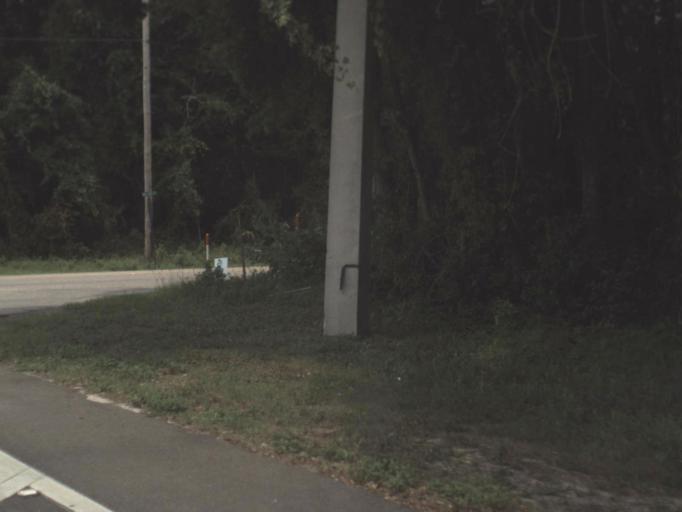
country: US
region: Florida
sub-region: Levy County
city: Chiefland
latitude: 29.4966
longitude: -82.8724
